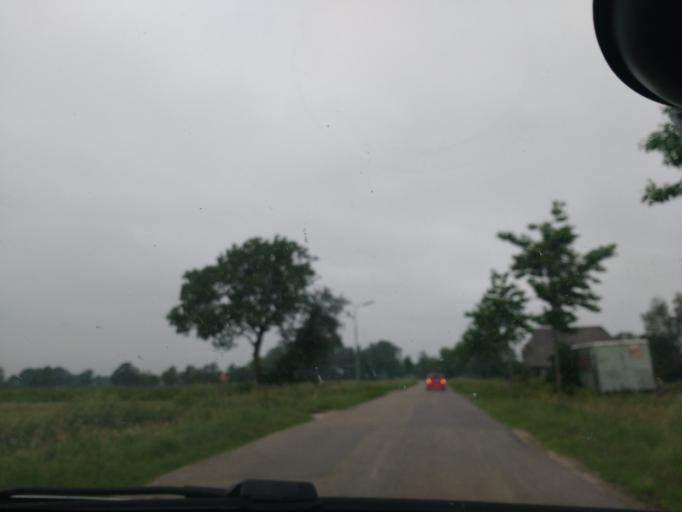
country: NL
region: Utrecht
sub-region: Gemeente Rhenen
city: Rhenen
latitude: 51.9675
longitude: 5.6135
